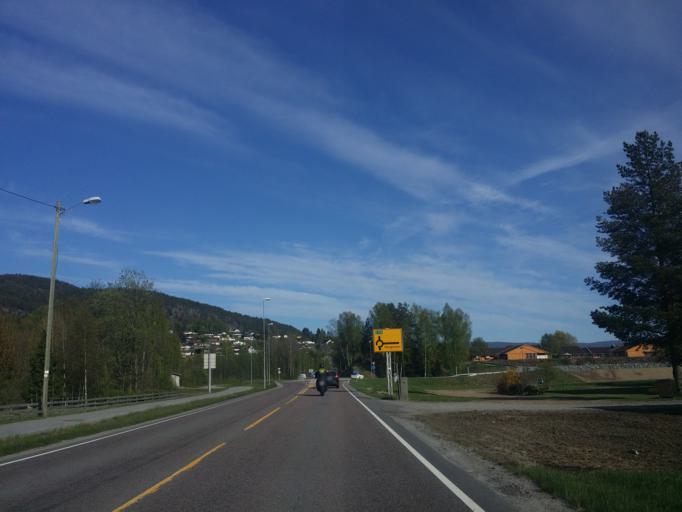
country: NO
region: Telemark
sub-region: Notodden
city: Notodden
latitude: 59.5768
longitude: 9.1877
